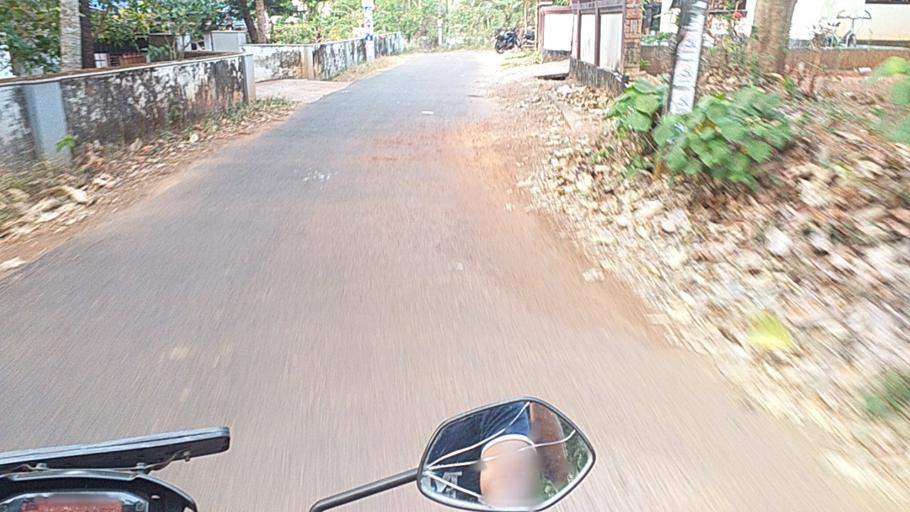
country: IN
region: Kerala
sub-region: Thrissur District
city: Kunnamkulam
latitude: 10.7427
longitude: 76.0410
